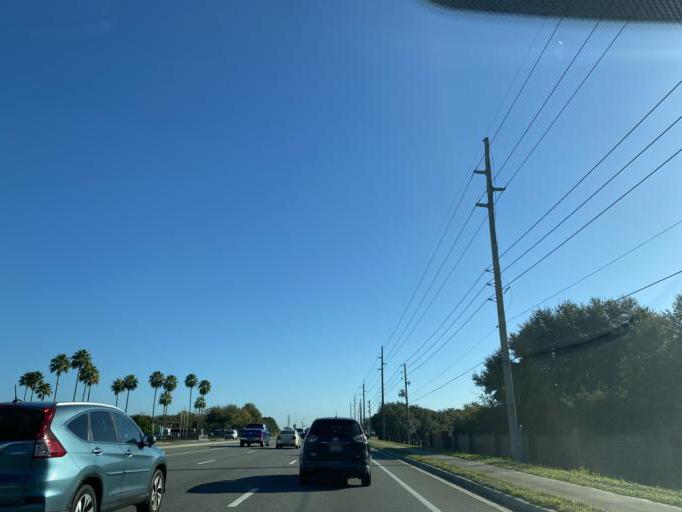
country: US
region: Florida
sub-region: Orange County
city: Oakland
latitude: 28.5462
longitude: -81.6482
